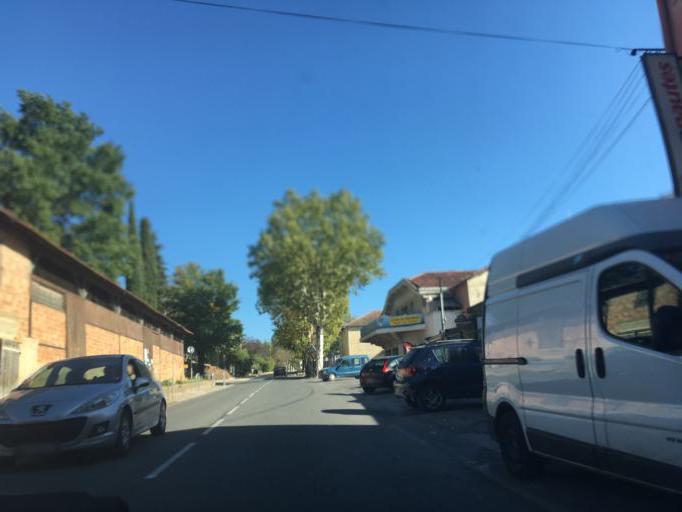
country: FR
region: Provence-Alpes-Cote d'Azur
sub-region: Departement du Var
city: Salernes
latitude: 43.5620
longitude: 6.2367
